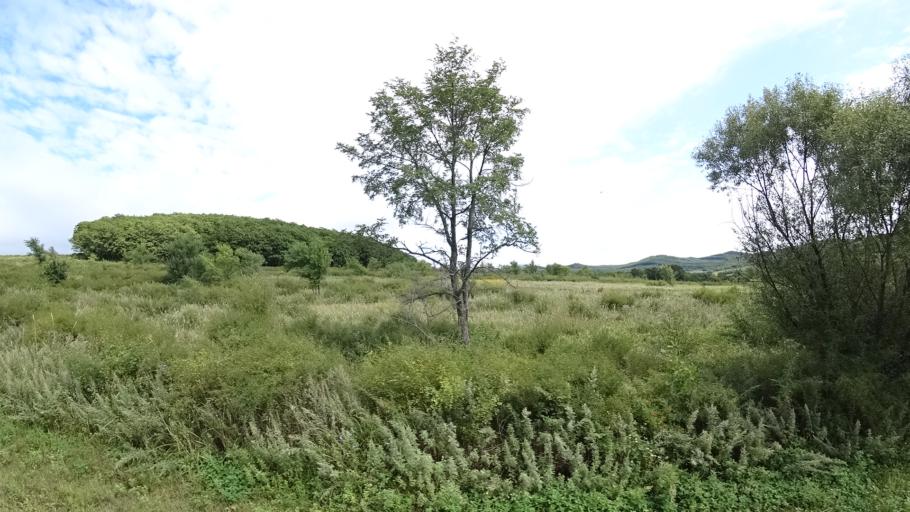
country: RU
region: Primorskiy
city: Lyalichi
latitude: 44.1405
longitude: 132.3883
